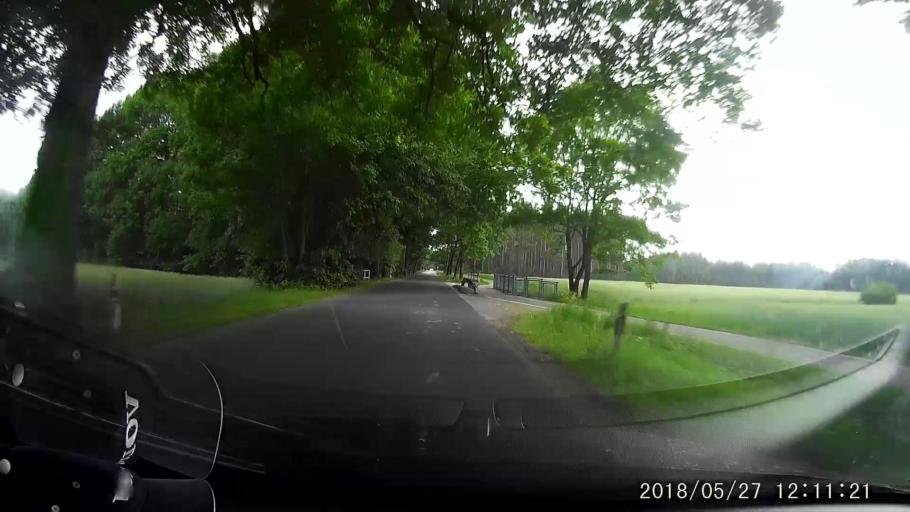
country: DE
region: Saxony
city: Klitten
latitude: 51.3576
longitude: 14.5747
